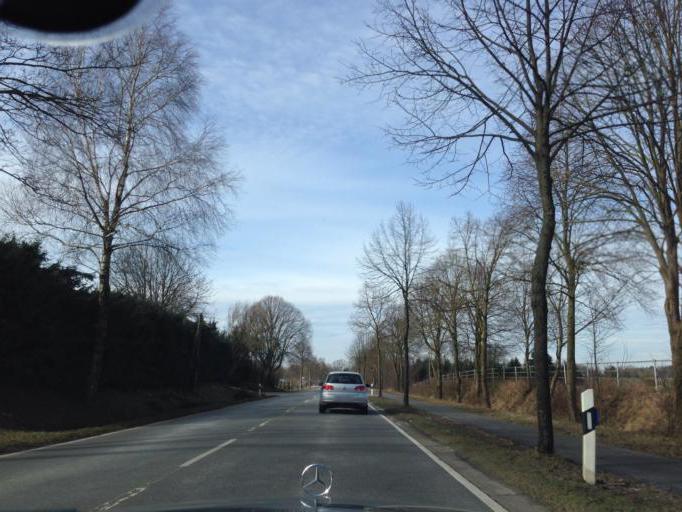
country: DE
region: Lower Saxony
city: Seevetal
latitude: 53.4390
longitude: 9.9109
